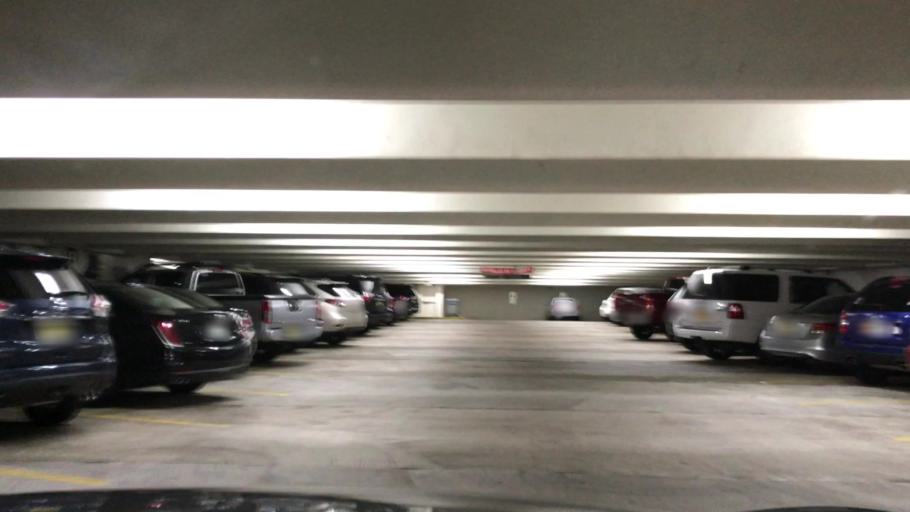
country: US
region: New Jersey
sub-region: Atlantic County
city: Atlantic City
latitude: 39.3603
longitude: -74.4389
